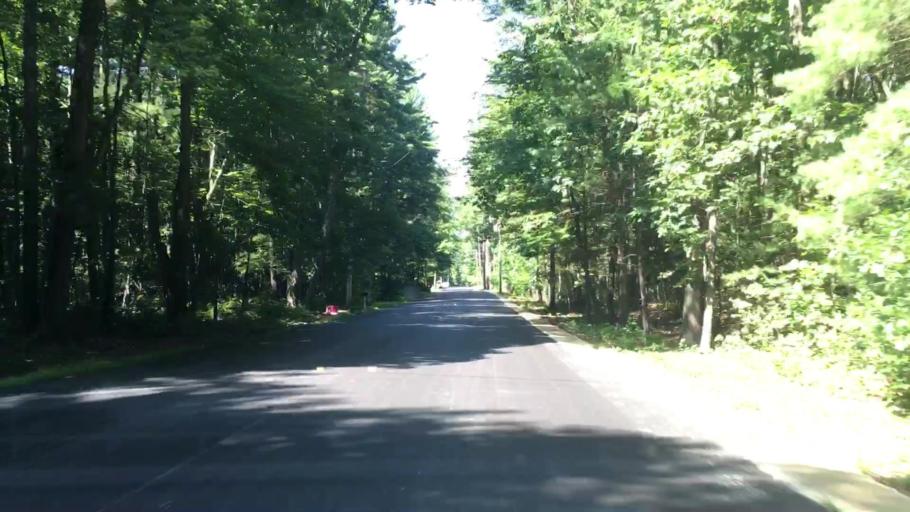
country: US
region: Maine
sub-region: York County
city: Eliot
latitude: 43.1615
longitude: -70.8394
